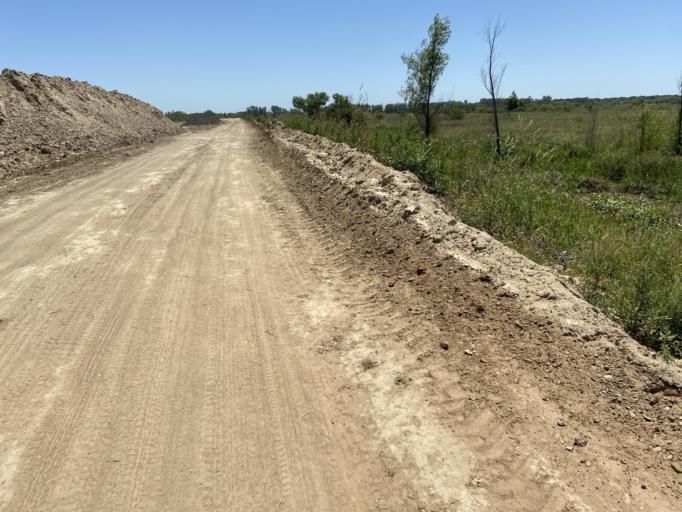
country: AR
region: Entre Rios
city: Villa Paranacito
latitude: -33.7108
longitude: -58.6502
